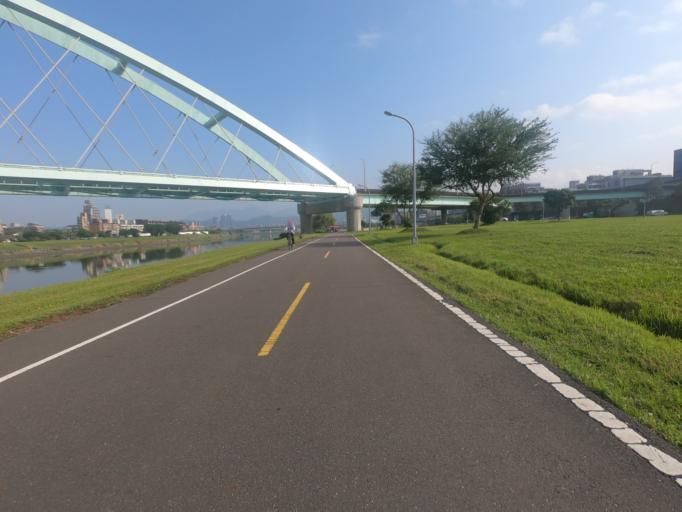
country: TW
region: Taipei
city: Taipei
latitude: 25.0557
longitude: 121.5725
